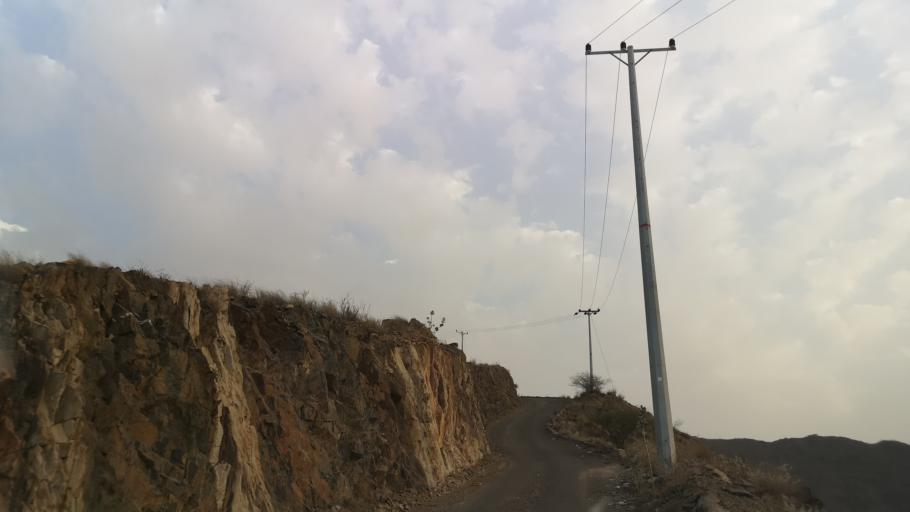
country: YE
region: Sa'dah
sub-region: Monabbih
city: Suq al Khamis
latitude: 17.3266
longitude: 43.1455
